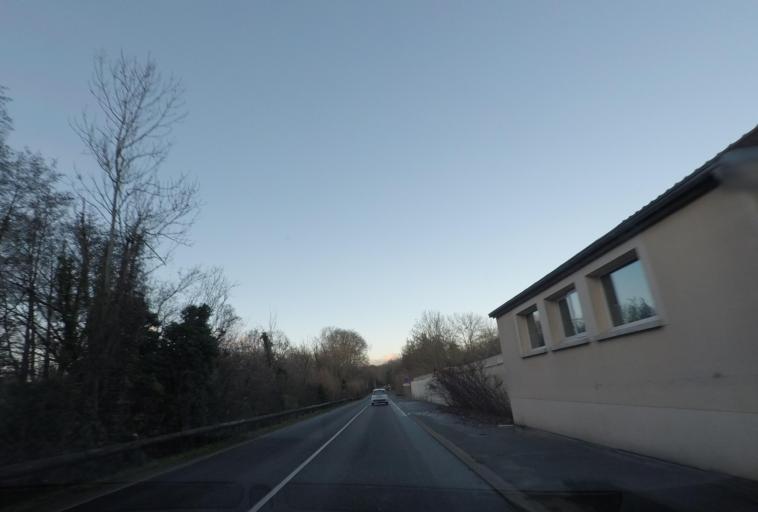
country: FR
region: Ile-de-France
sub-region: Departement de l'Essonne
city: Mennecy
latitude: 48.5750
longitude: 2.4343
